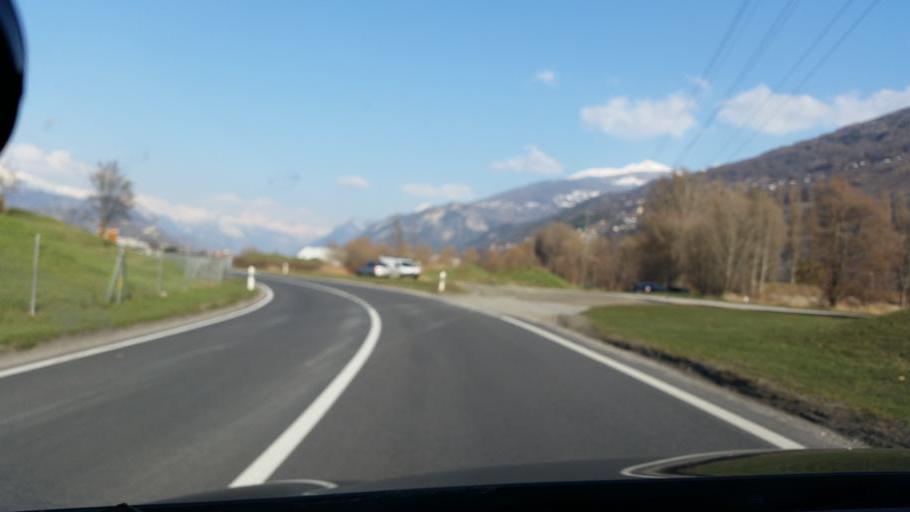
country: CH
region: Valais
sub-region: Conthey District
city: Conthey
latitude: 46.2129
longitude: 7.3178
